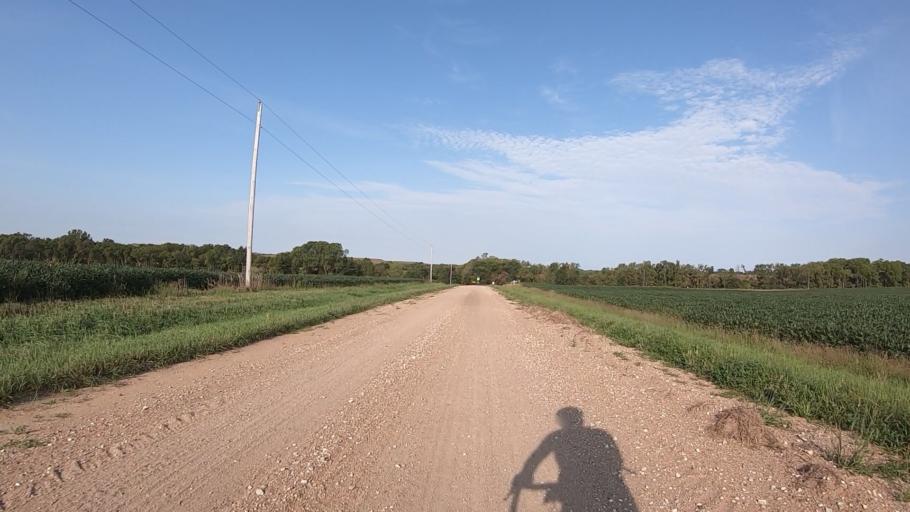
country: US
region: Kansas
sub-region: Marshall County
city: Blue Rapids
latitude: 39.6534
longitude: -96.8603
